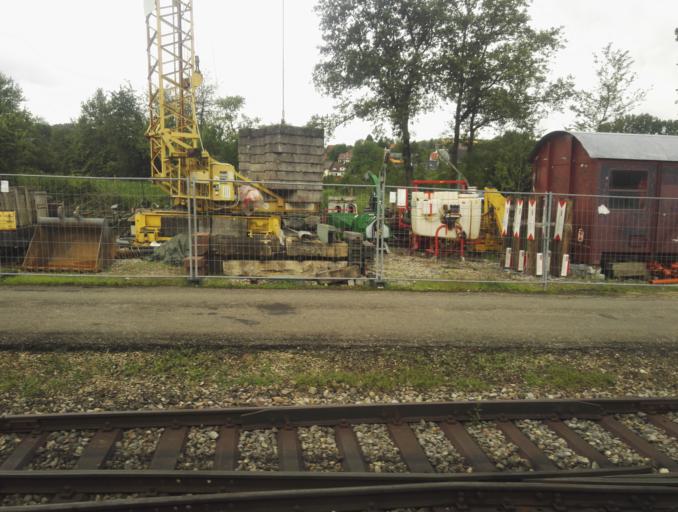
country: DE
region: Baden-Wuerttemberg
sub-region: Freiburg Region
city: Blumberg
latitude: 47.8093
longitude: 8.5349
